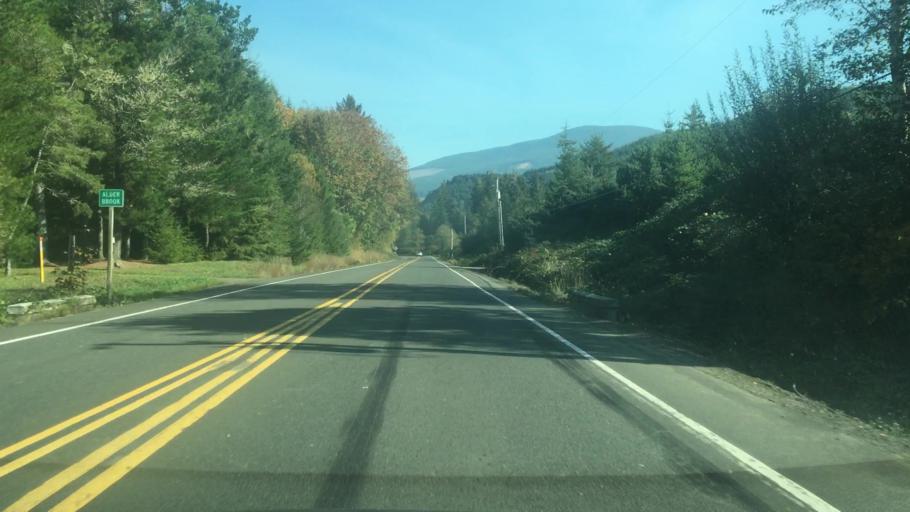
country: US
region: Oregon
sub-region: Lincoln County
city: Rose Lodge
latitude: 45.0212
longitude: -123.8539
